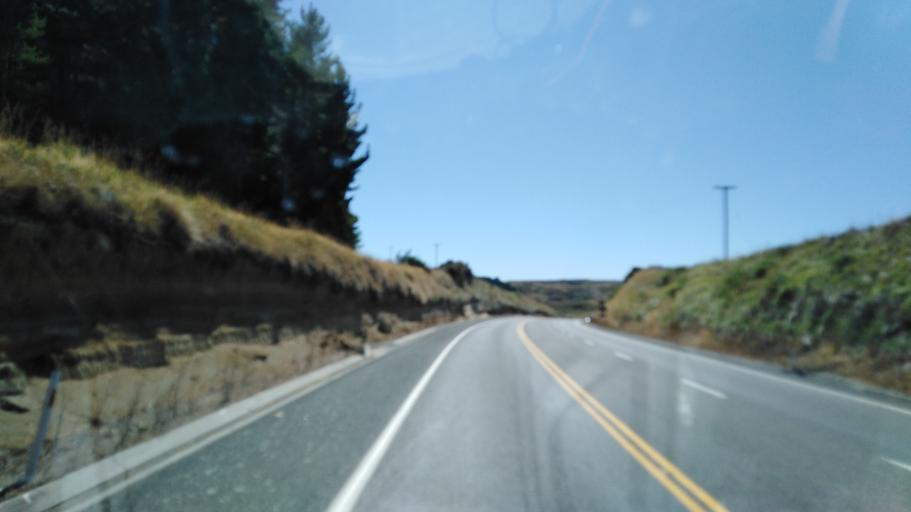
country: NZ
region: Manawatu-Wanganui
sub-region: Ruapehu District
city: Waiouru
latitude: -39.4497
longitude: 175.6783
